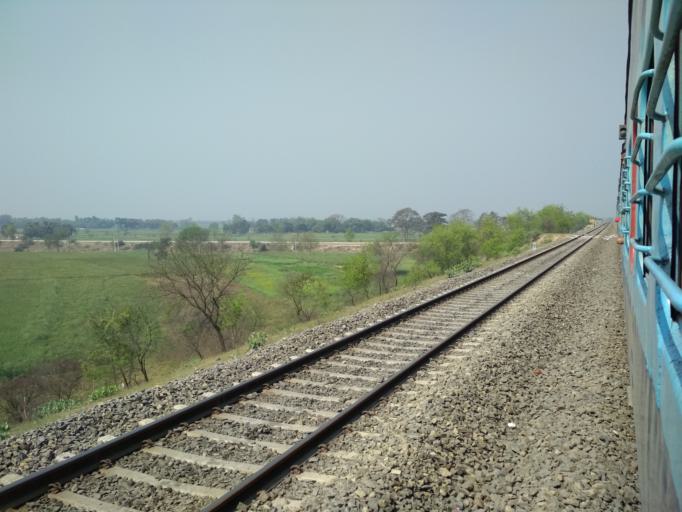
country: IN
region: Bihar
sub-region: Munger
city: Munger
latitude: 25.4363
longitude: 86.4353
